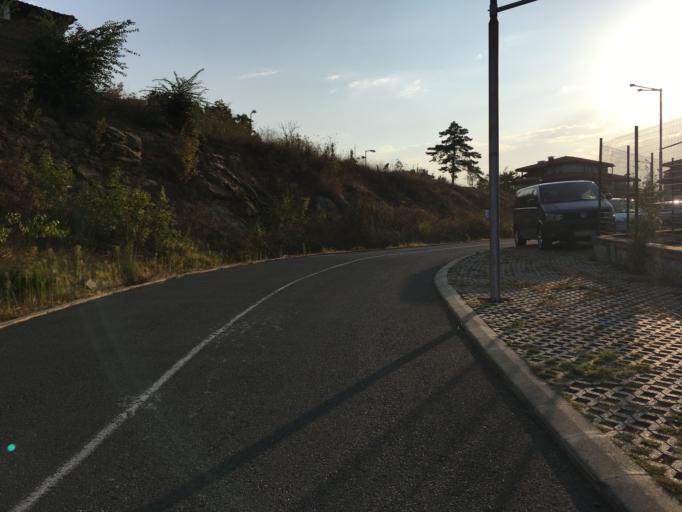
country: BG
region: Burgas
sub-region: Obshtina Sozopol
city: Sozopol
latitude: 42.4101
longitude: 27.6811
